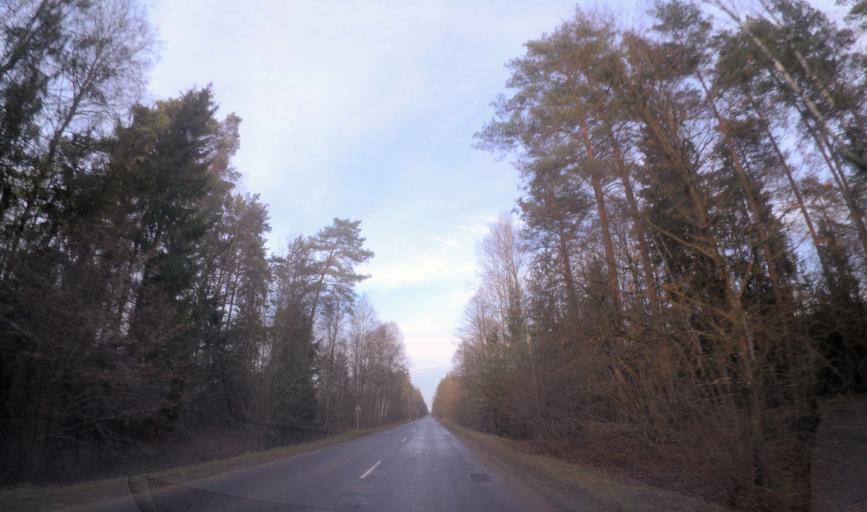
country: BY
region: Grodnenskaya
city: Hrodna
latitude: 53.7795
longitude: 24.0038
